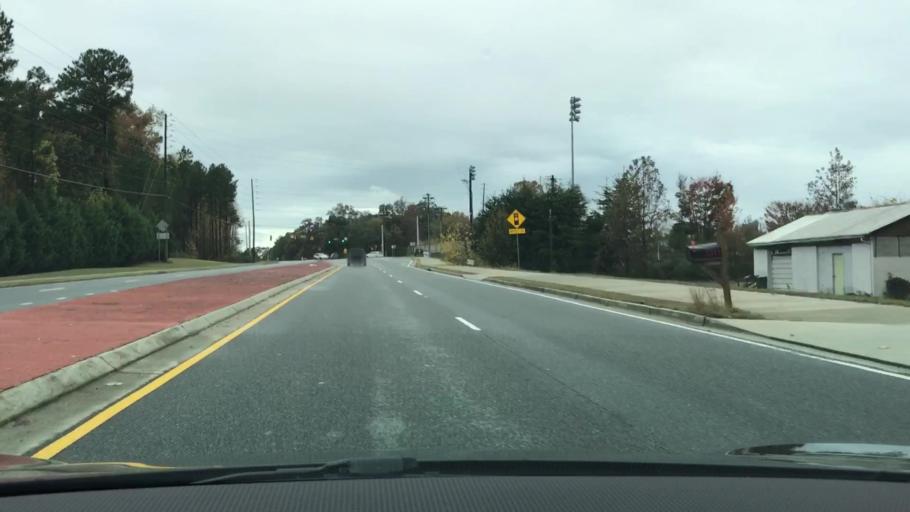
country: US
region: Georgia
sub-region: Gwinnett County
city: Suwanee
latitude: 34.1044
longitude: -84.1415
